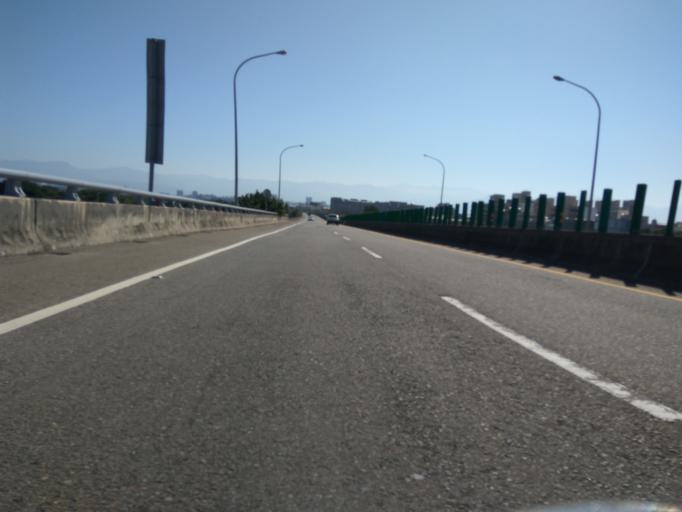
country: TW
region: Taiwan
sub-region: Hsinchu
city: Hsinchu
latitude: 24.8410
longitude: 120.9411
